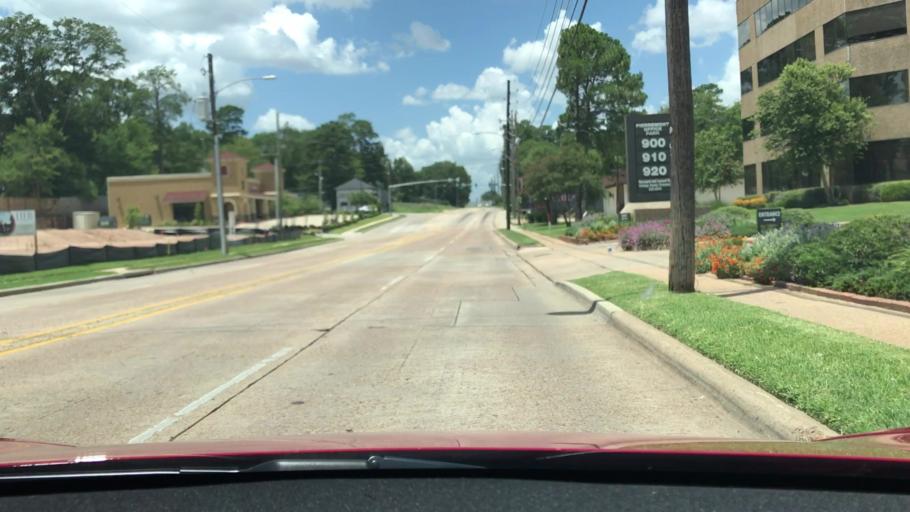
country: US
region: Louisiana
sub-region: Bossier Parish
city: Bossier City
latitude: 32.4548
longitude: -93.7483
